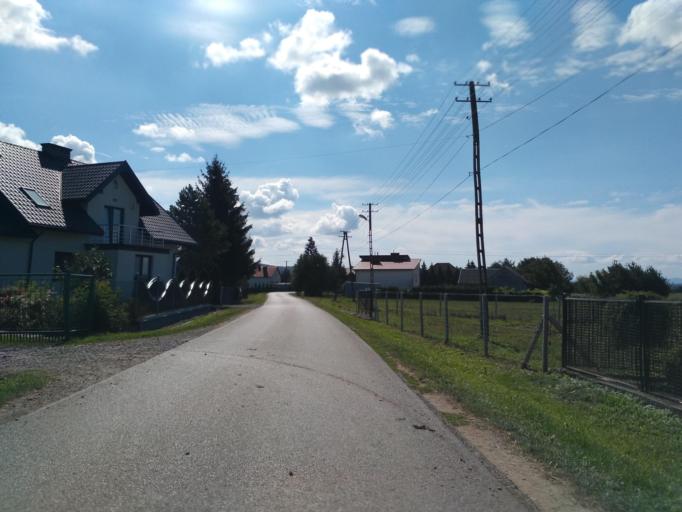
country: PL
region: Subcarpathian Voivodeship
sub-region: Powiat jasielski
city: Kolaczyce
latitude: 49.8110
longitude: 21.4148
